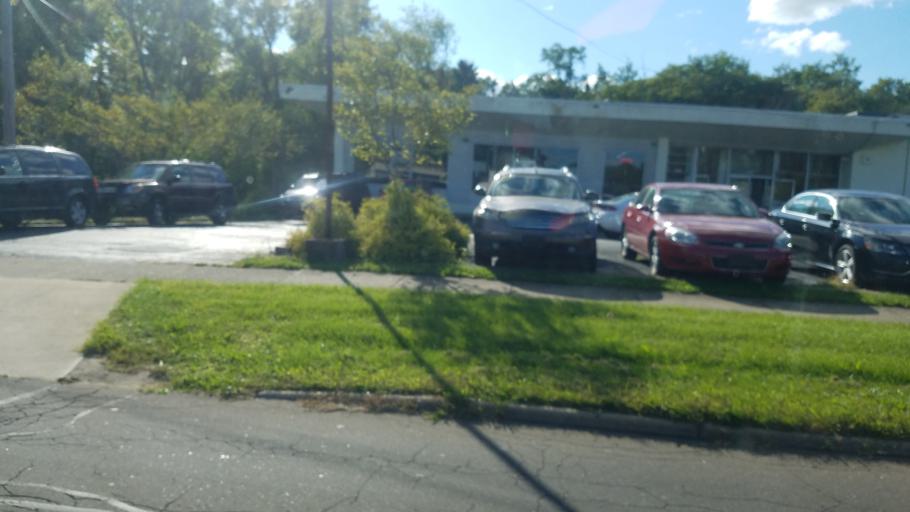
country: US
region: Ohio
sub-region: Mahoning County
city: Boardman
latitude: 41.0444
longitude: -80.6628
